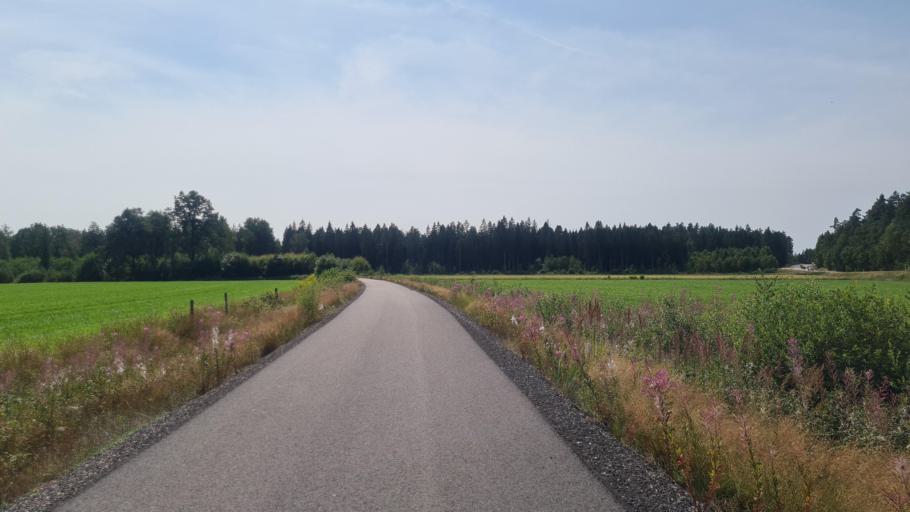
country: SE
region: Kronoberg
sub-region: Ljungby Kommun
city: Ljungby
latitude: 56.8672
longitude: 13.9771
